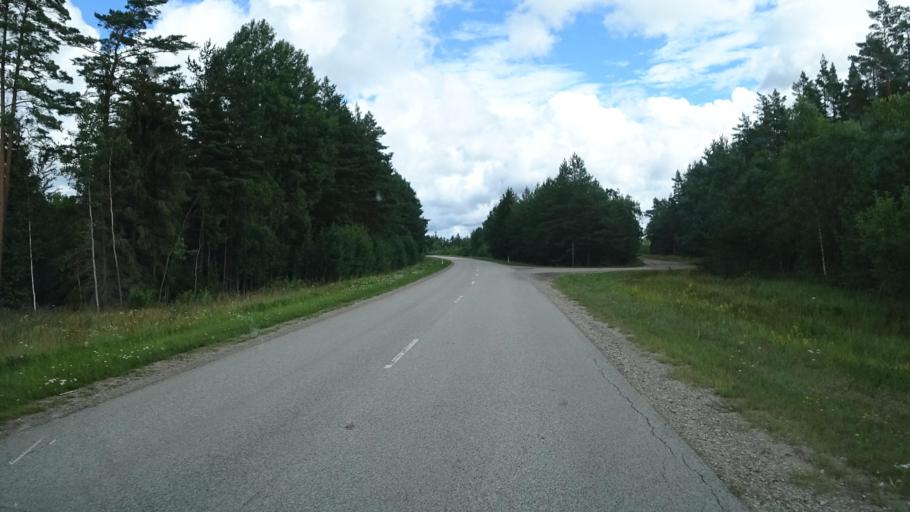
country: LV
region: Pavilostas
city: Pavilosta
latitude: 56.7483
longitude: 21.2501
